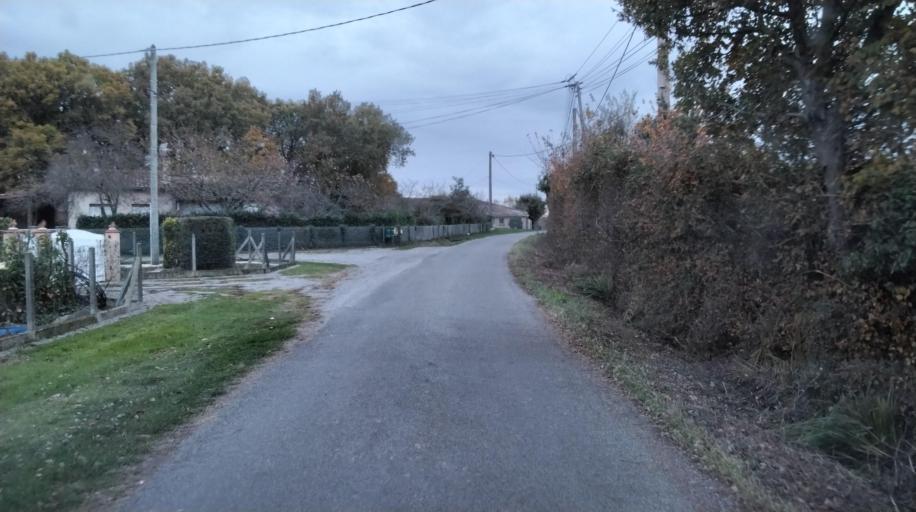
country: FR
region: Midi-Pyrenees
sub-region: Departement de la Haute-Garonne
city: Berat
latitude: 43.3927
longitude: 1.2049
